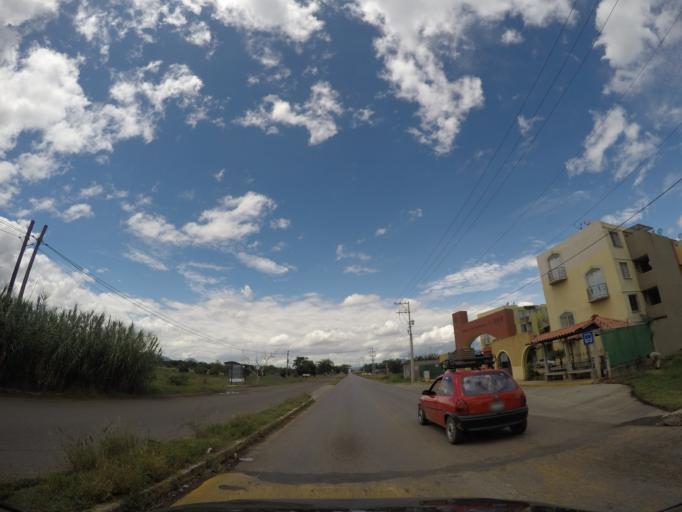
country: MX
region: Oaxaca
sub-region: Santa Cruz Xoxocotlan
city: San Isidro Monjas
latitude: 16.9942
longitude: -96.7429
